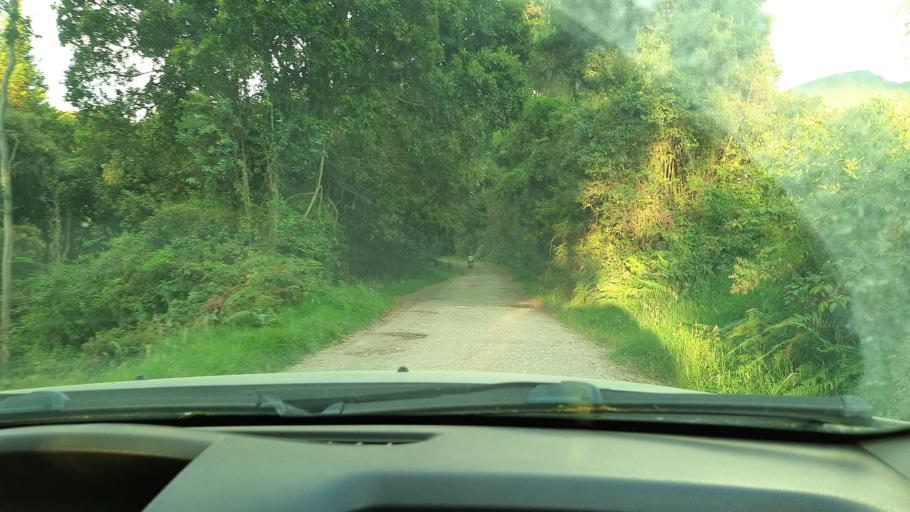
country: CO
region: Boyaca
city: La Capilla
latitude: 5.7133
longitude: -73.4779
